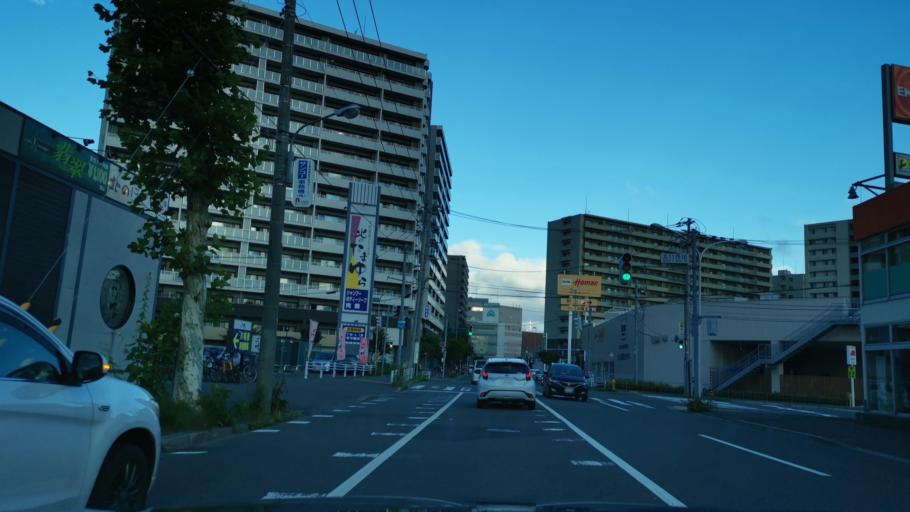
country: JP
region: Hokkaido
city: Sapporo
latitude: 43.0713
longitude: 141.3287
